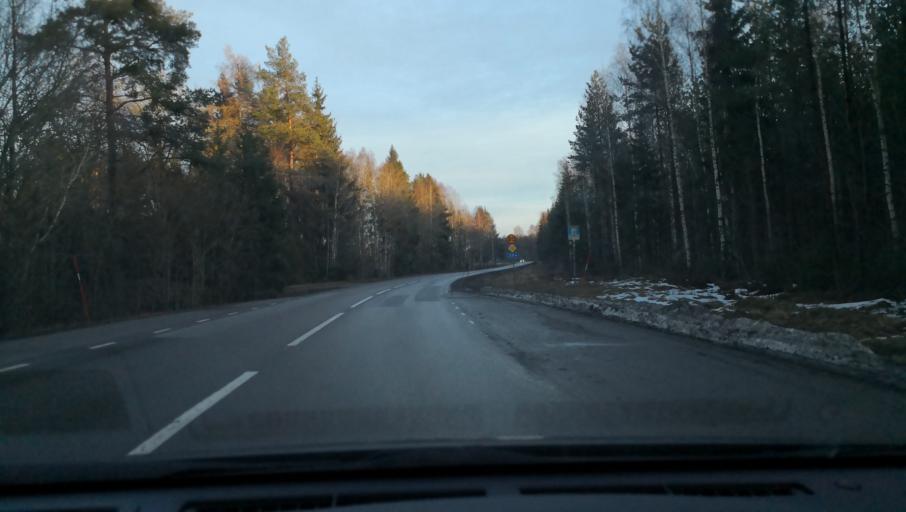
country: SE
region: OErebro
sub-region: Lekebergs Kommun
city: Fjugesta
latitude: 59.1609
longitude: 14.7721
